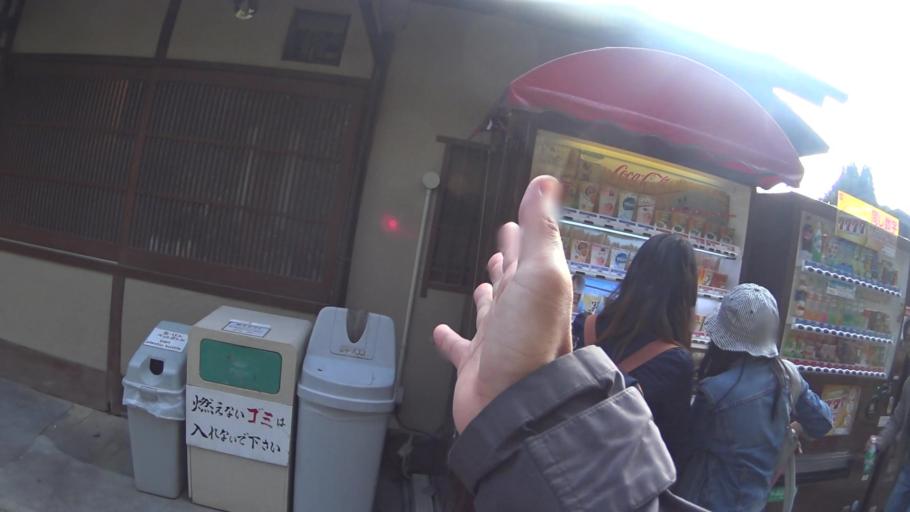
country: JP
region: Kyoto
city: Kyoto
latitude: 35.0330
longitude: 135.7199
